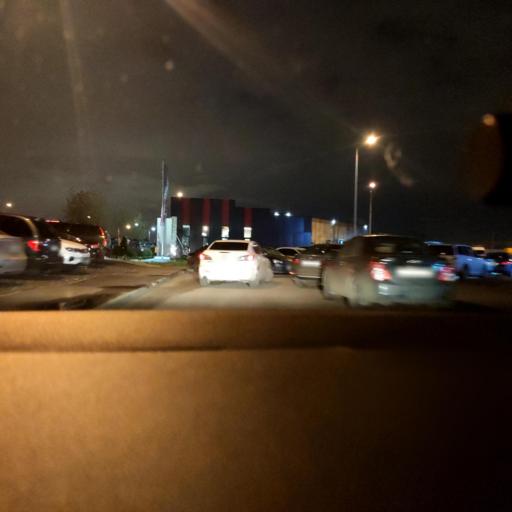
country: RU
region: Moskovskaya
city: Kotel'niki
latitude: 55.6386
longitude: 37.8471
